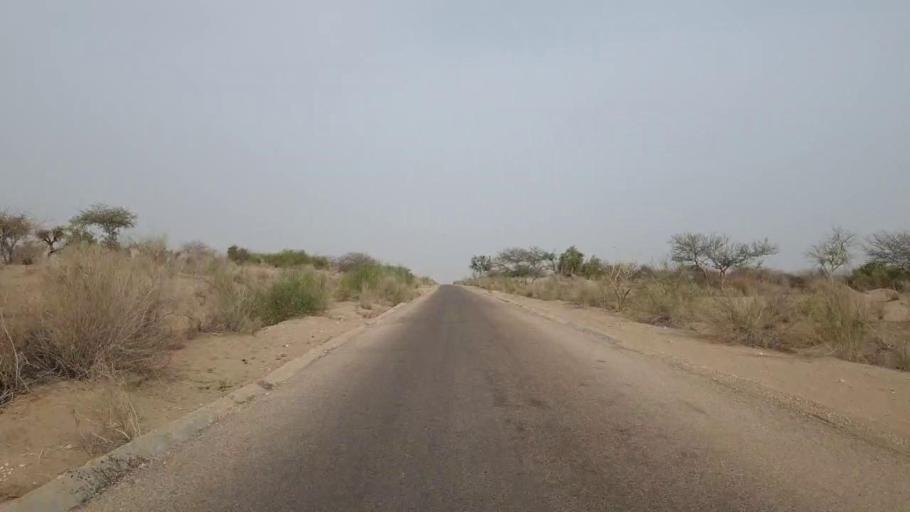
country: PK
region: Sindh
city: Islamkot
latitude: 24.5601
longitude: 70.3415
